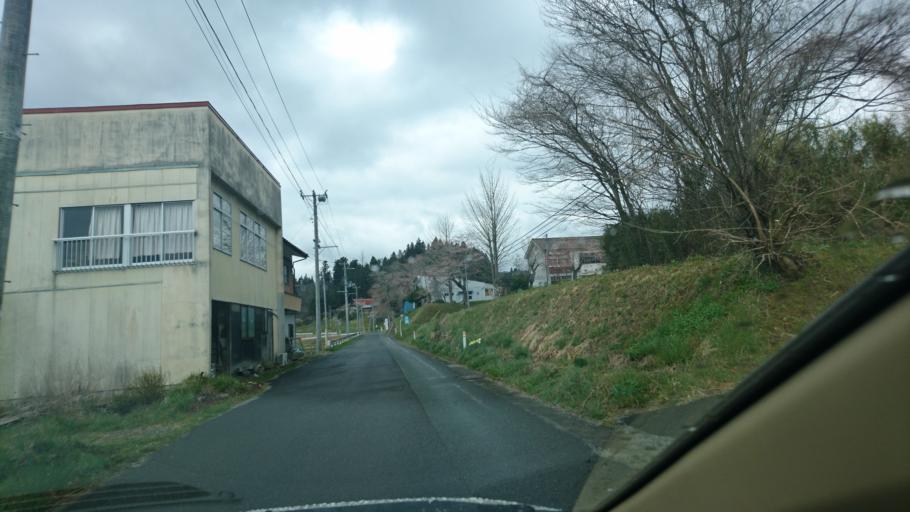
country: JP
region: Iwate
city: Ichinoseki
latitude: 38.9449
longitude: 141.3224
